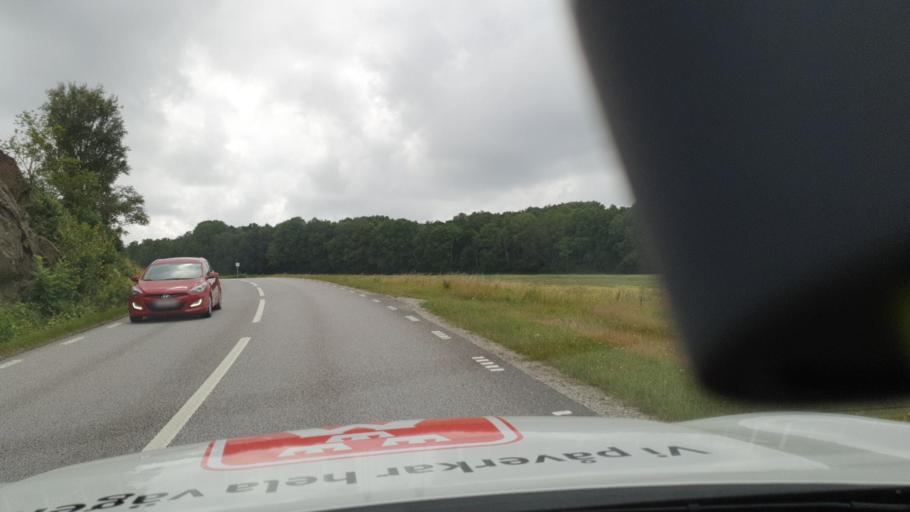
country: SE
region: Vaestra Goetaland
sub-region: Tanums Kommun
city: Grebbestad
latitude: 58.7159
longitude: 11.2655
